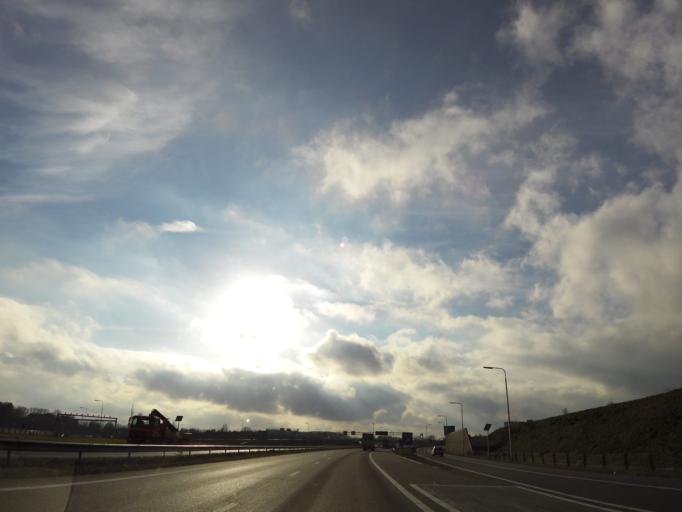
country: NL
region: Limburg
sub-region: Gemeente Roerdalen
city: Melick
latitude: 51.1843
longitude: 6.0239
